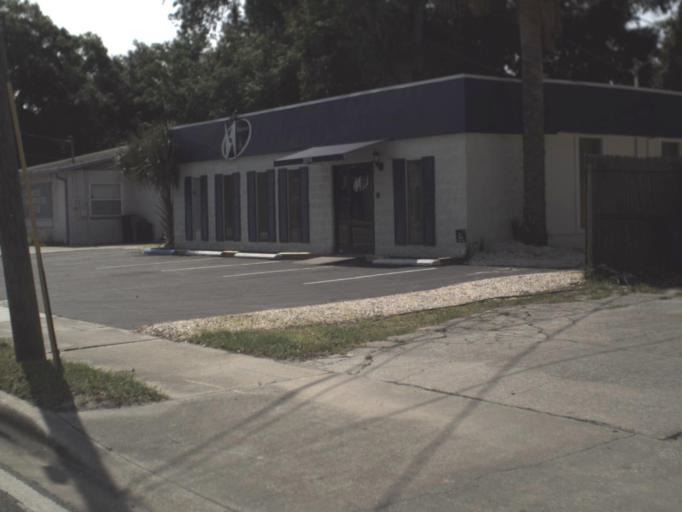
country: US
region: Florida
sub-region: Duval County
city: Jacksonville
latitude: 30.2608
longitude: -81.6366
